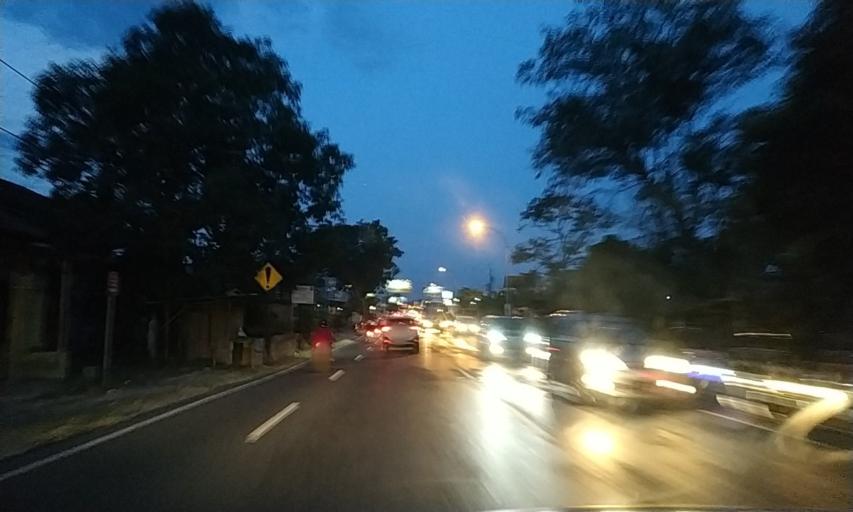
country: ID
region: Daerah Istimewa Yogyakarta
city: Godean
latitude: -7.8129
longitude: 110.2653
